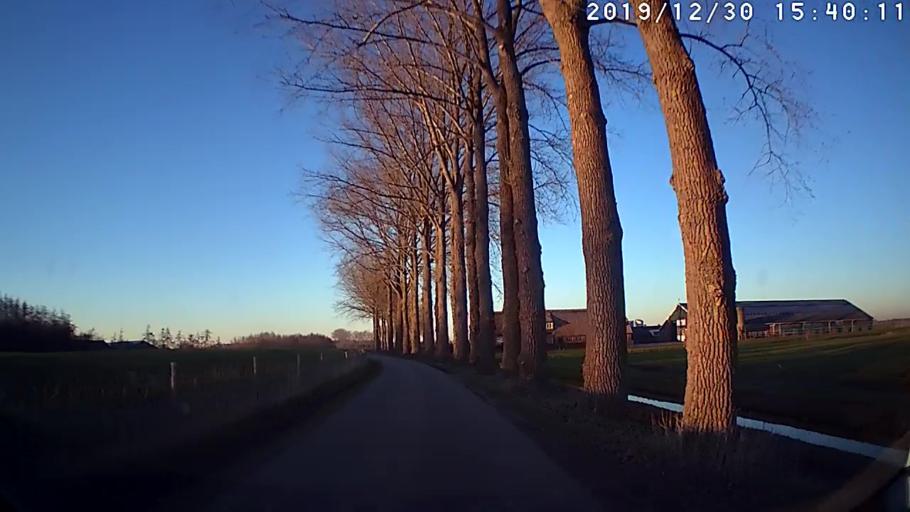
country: NL
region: Overijssel
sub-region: Gemeente Zwolle
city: Zwolle
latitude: 52.4616
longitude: 6.1516
